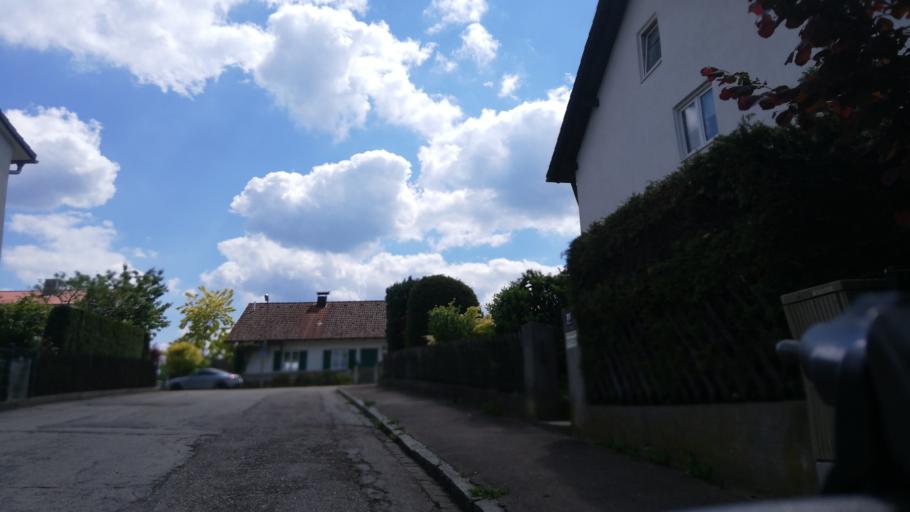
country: DE
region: Bavaria
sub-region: Upper Bavaria
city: Pfaffenhofen an der Ilm
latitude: 48.5226
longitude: 11.5173
